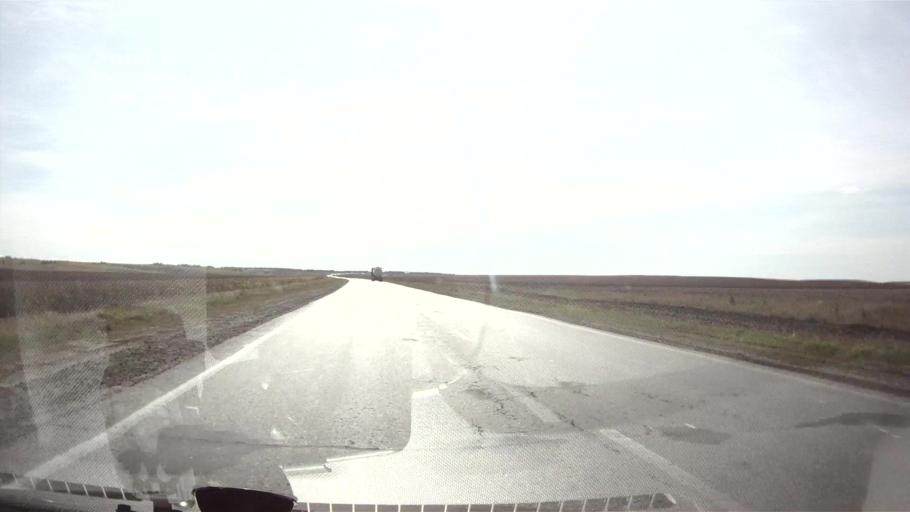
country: RU
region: Samara
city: Varlamovo
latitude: 53.0271
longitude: 48.3337
